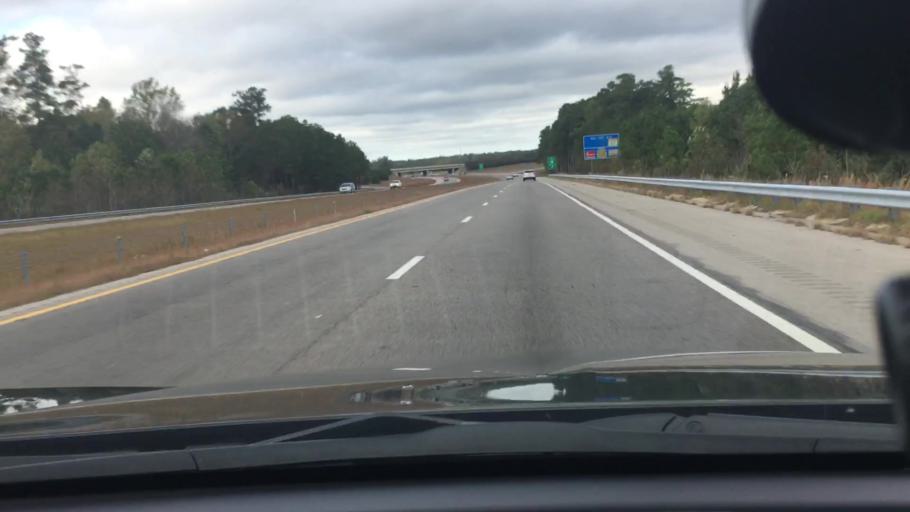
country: US
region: North Carolina
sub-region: Wilson County
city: Lucama
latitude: 35.7552
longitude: -78.0247
